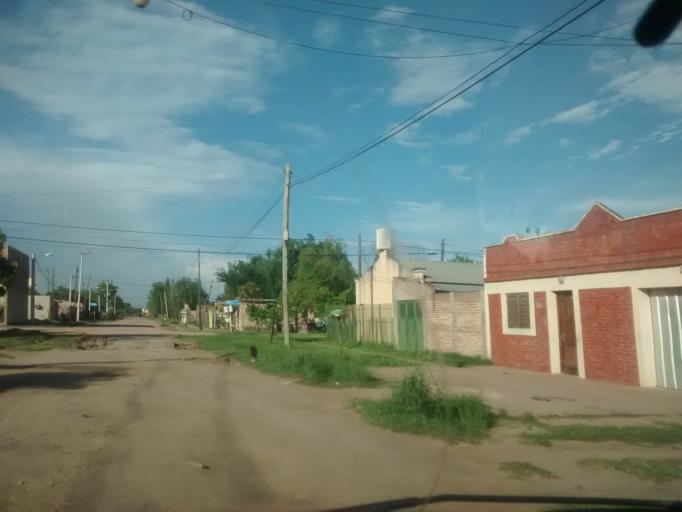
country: AR
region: Chaco
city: Fontana
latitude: -27.4573
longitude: -59.0305
